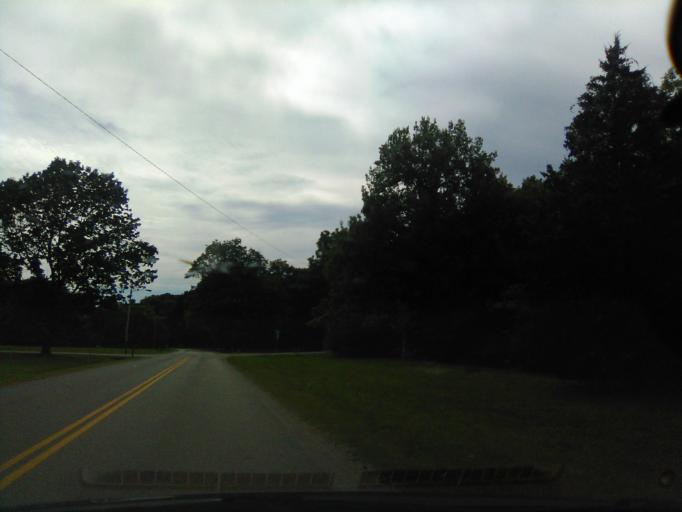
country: US
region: Tennessee
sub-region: Davidson County
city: Belle Meade
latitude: 36.1035
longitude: -86.8894
